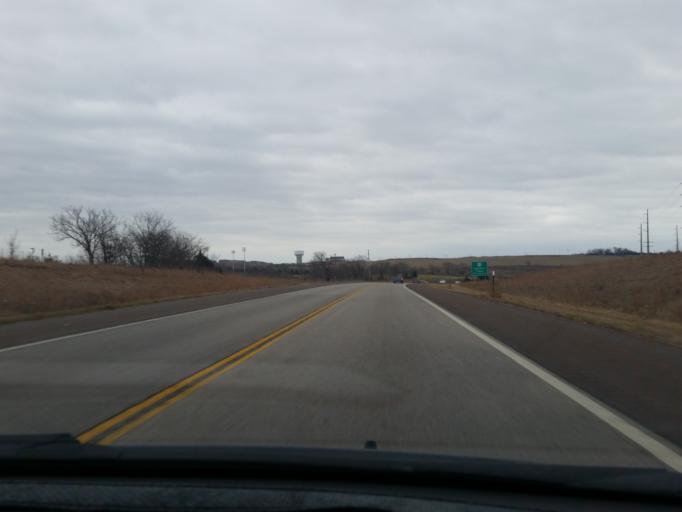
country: US
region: Kansas
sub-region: Douglas County
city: Lawrence
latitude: 38.9843
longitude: -95.3381
